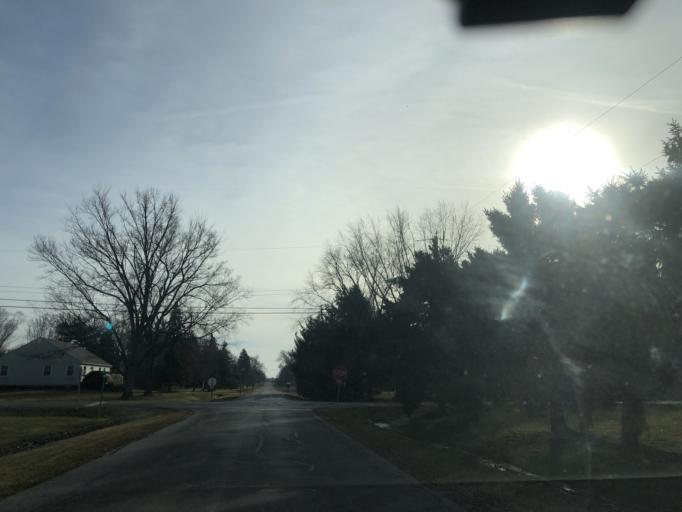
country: US
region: Illinois
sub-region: Cook County
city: Lemont
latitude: 41.7115
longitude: -88.0099
